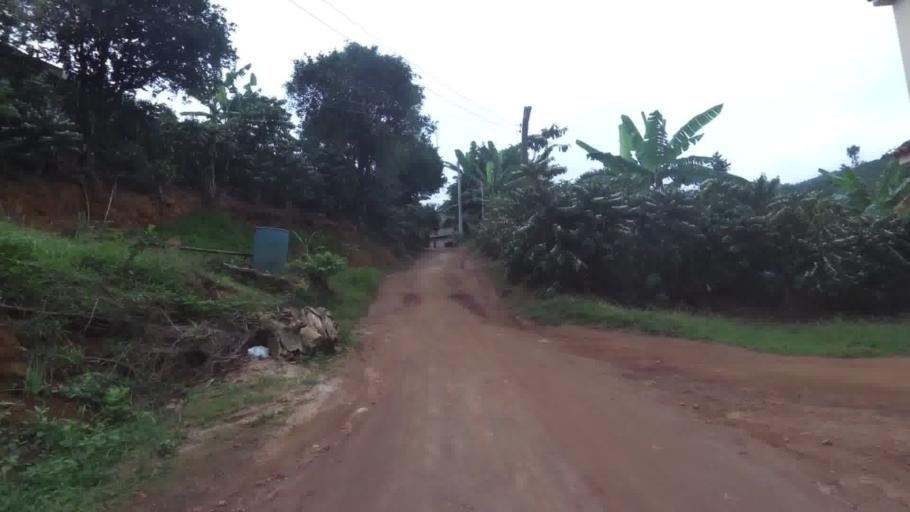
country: BR
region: Espirito Santo
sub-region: Iconha
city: Iconha
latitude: -20.7602
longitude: -40.8371
